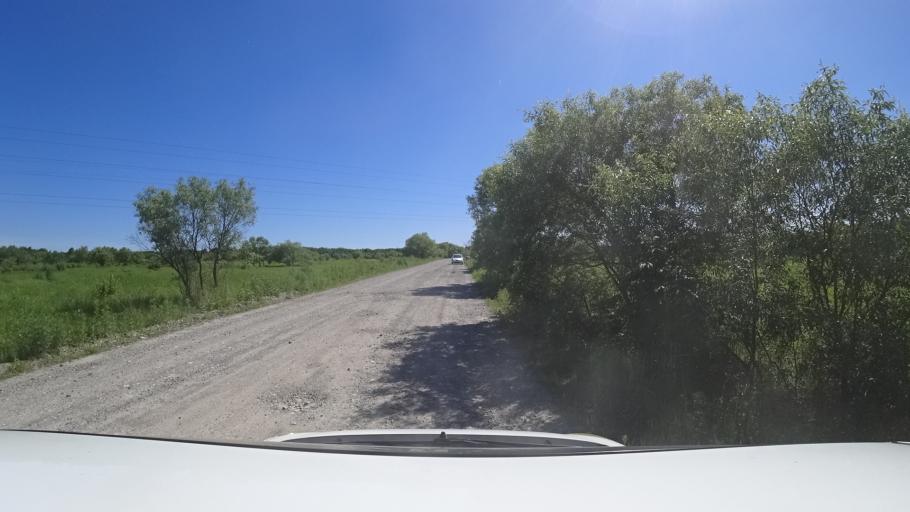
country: RU
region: Khabarovsk Krai
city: Topolevo
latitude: 48.5639
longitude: 135.1969
